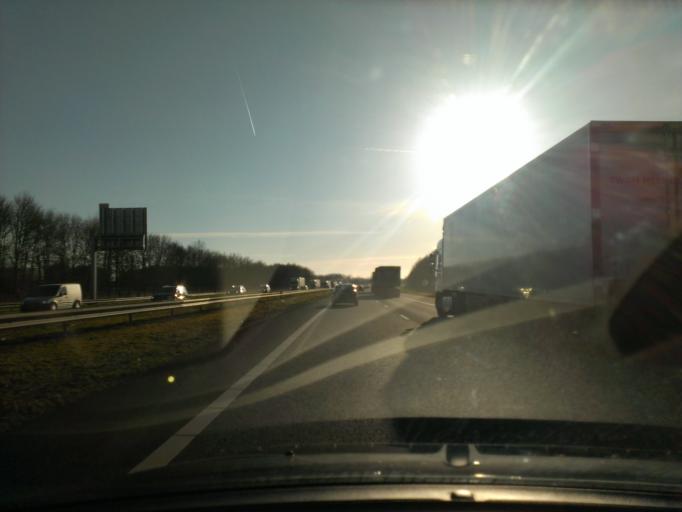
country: NL
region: Overijssel
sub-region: Gemeente Almelo
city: Almelo
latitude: 52.3024
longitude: 6.6749
